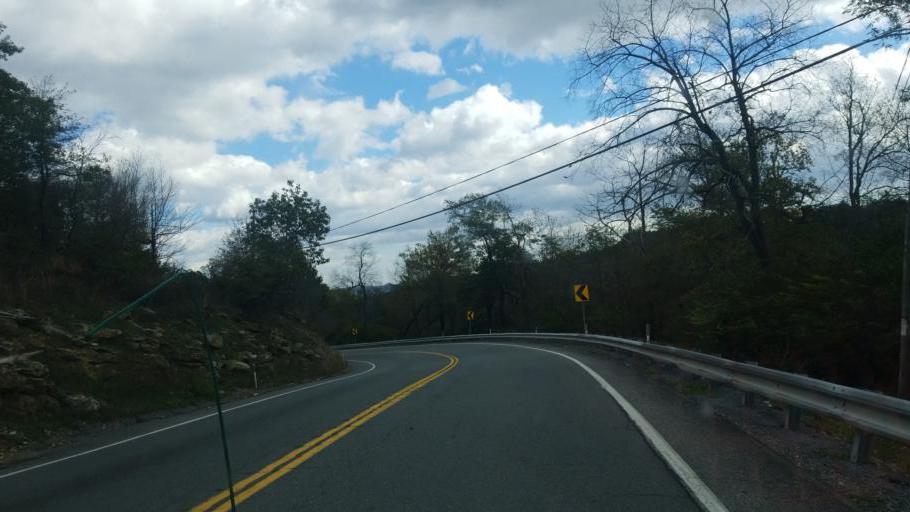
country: US
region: Pennsylvania
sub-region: Fulton County
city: McConnellsburg
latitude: 39.9180
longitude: -77.9488
